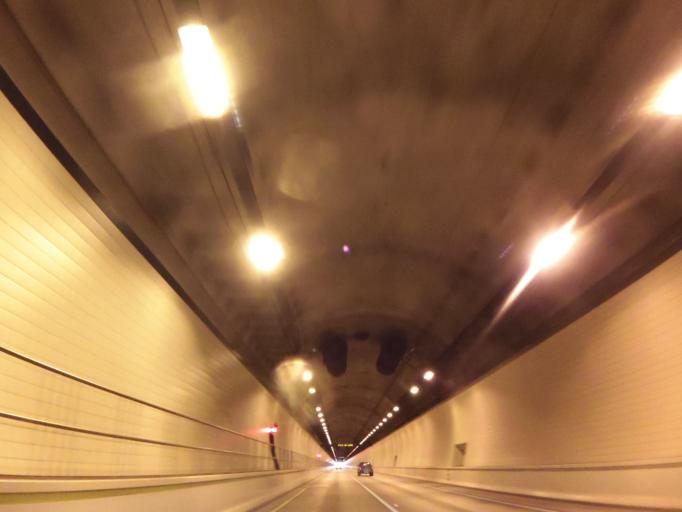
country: US
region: Tennessee
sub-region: Claiborne County
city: Harrogate
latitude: 36.6027
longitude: -83.6834
